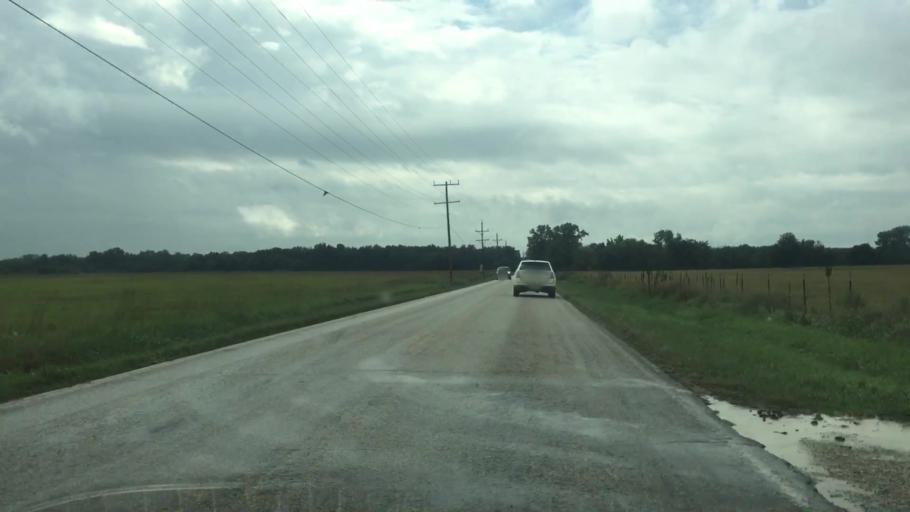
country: US
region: Kansas
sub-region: Allen County
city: Iola
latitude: 37.8747
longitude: -95.4369
